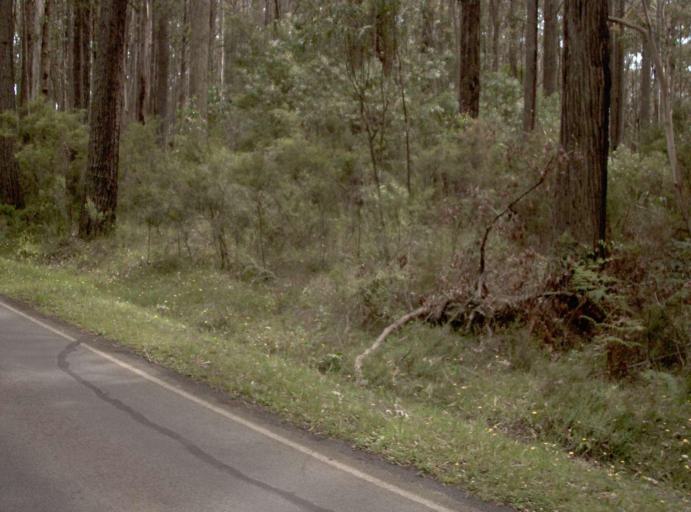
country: AU
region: Victoria
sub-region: Latrobe
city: Moe
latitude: -37.9918
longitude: 146.4097
